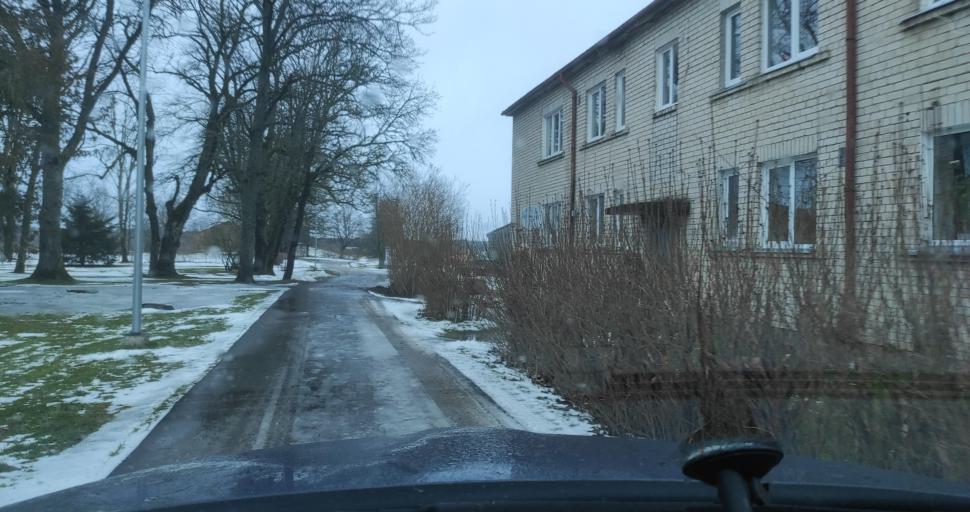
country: LV
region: Dundaga
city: Dundaga
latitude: 57.5130
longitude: 22.0239
